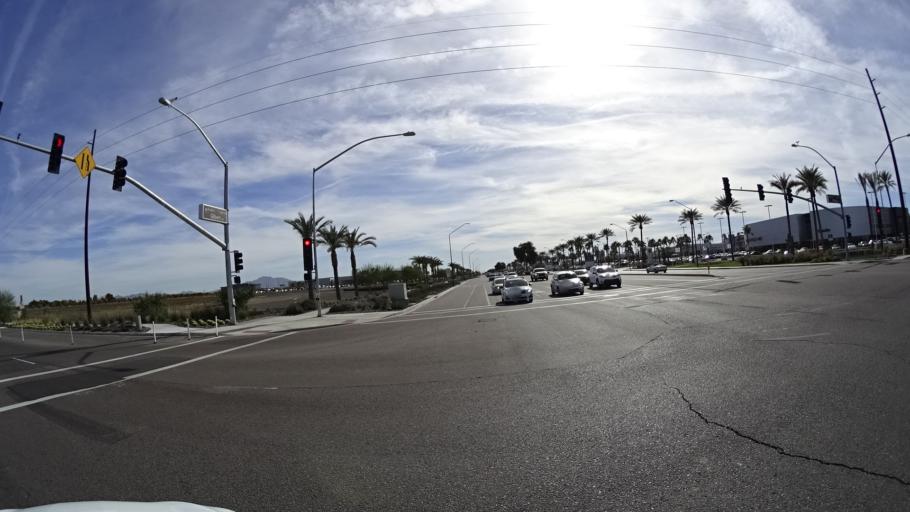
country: US
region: Arizona
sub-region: Maricopa County
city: Chandler
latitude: 33.2920
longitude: -111.7896
